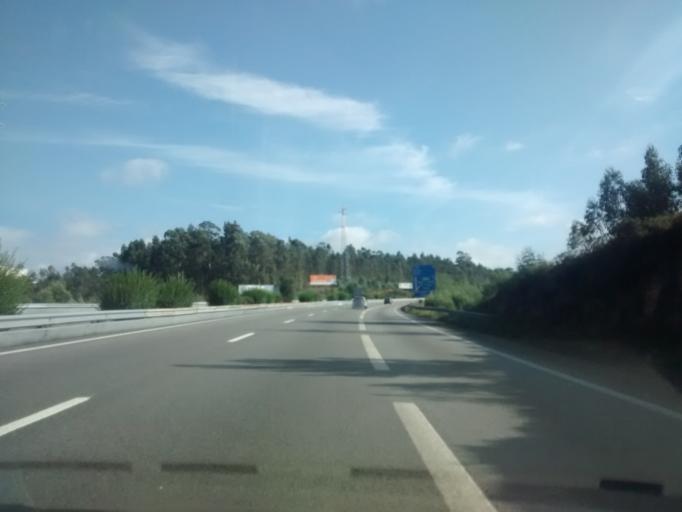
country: PT
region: Porto
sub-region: Santo Tirso
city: Santo Tirso
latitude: 41.3472
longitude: -8.5060
